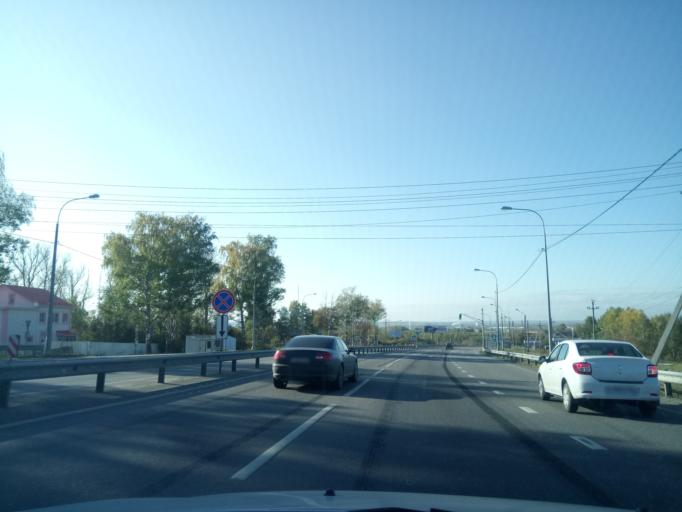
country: RU
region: Nizjnij Novgorod
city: Burevestnik
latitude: 56.1884
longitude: 43.9239
